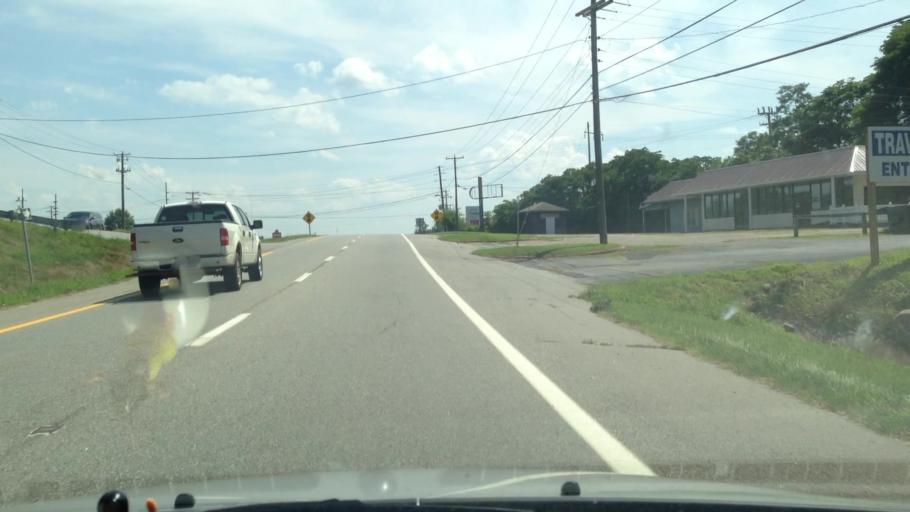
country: US
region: Virginia
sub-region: Henry County
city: Chatmoss
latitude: 36.6312
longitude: -79.8594
